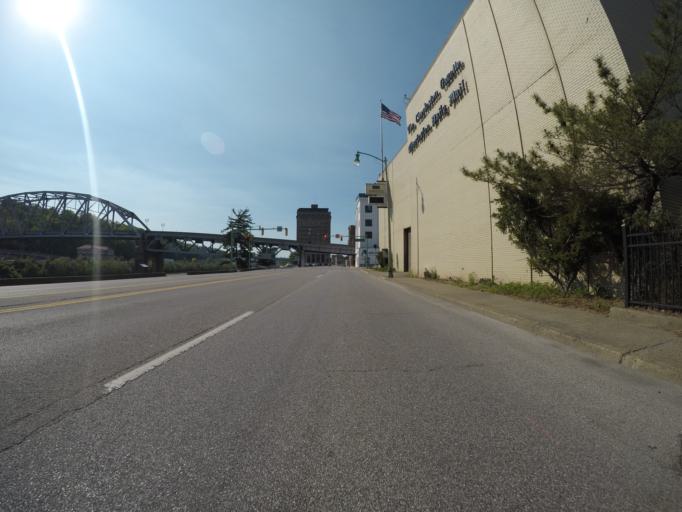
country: US
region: West Virginia
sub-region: Kanawha County
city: Charleston
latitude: 38.3469
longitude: -81.6352
